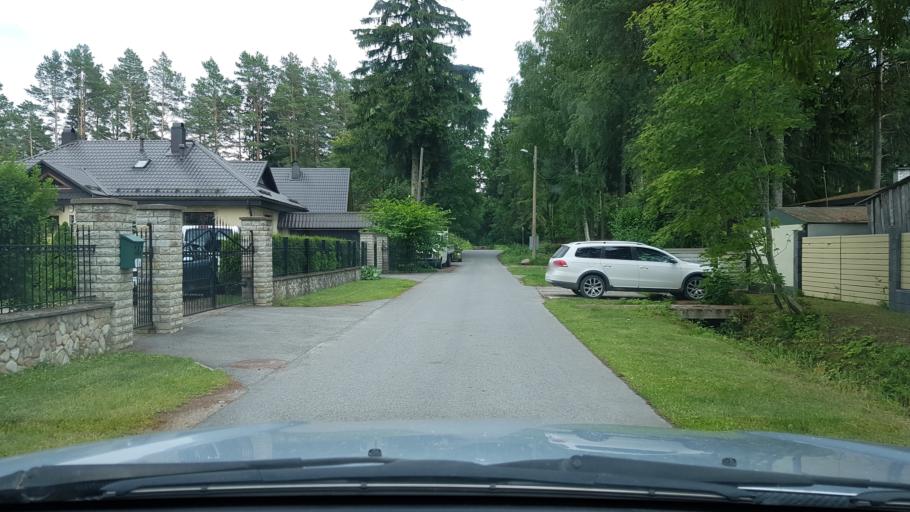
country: EE
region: Ida-Virumaa
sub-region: Narva-Joesuu linn
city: Narva-Joesuu
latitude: 59.4497
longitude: 28.0280
